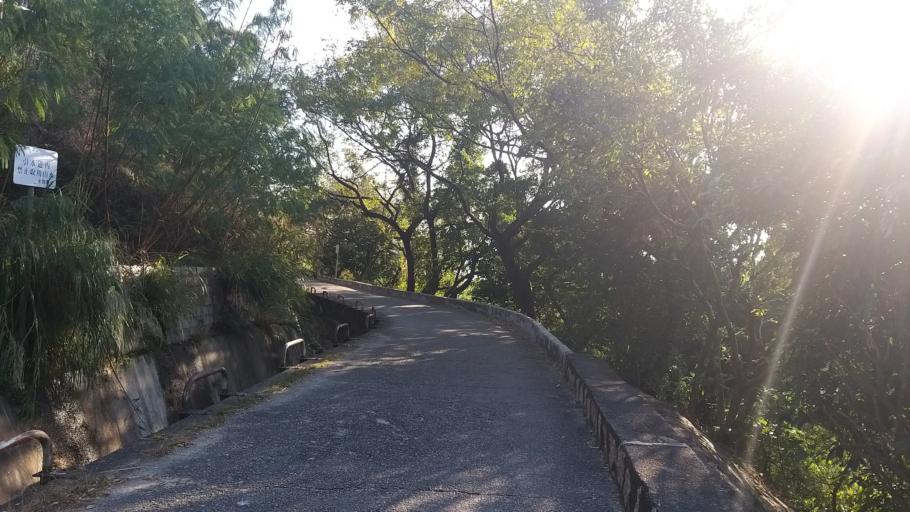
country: HK
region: Tuen Mun
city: Tuen Mun
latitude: 22.3913
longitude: 113.9832
